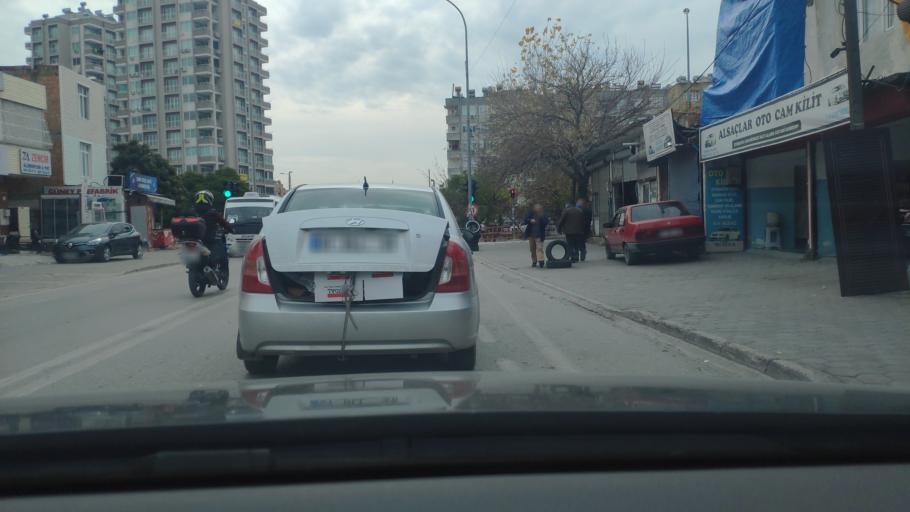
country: TR
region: Adana
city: Adana
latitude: 37.0109
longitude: 35.3151
